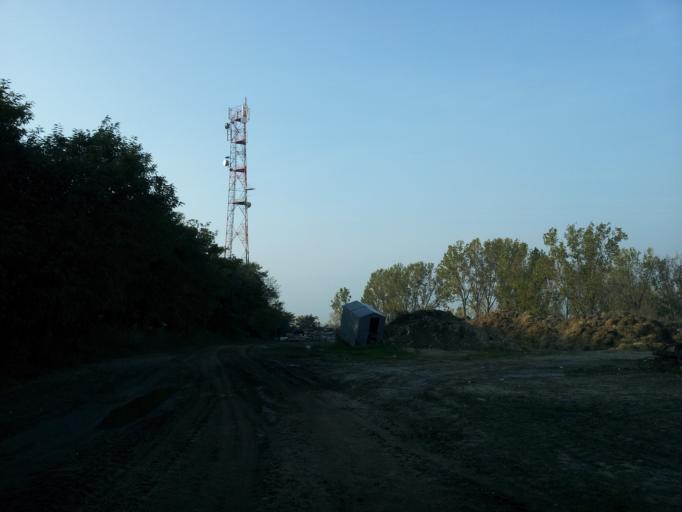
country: HU
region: Komarom-Esztergom
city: Kisber
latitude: 47.4874
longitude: 18.0453
